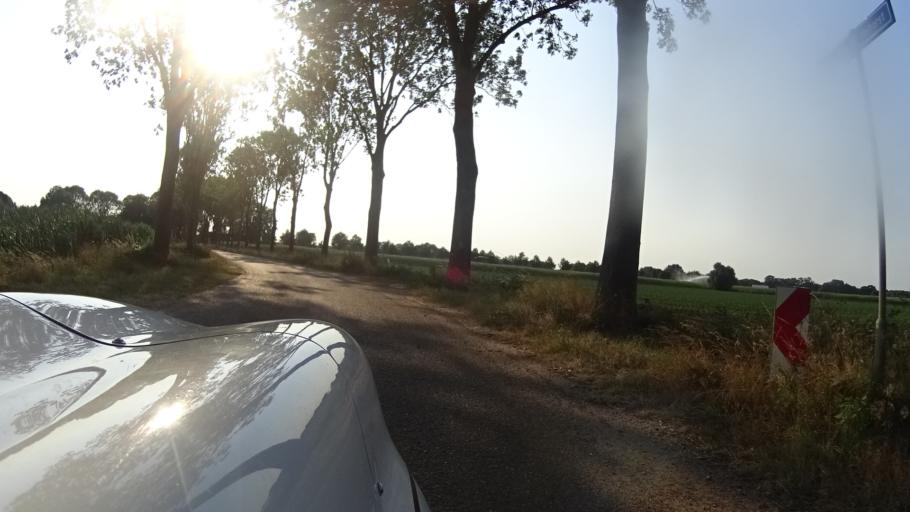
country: NL
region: North Brabant
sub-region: Gemeente Landerd
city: Zeeland
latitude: 51.7133
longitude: 5.6897
